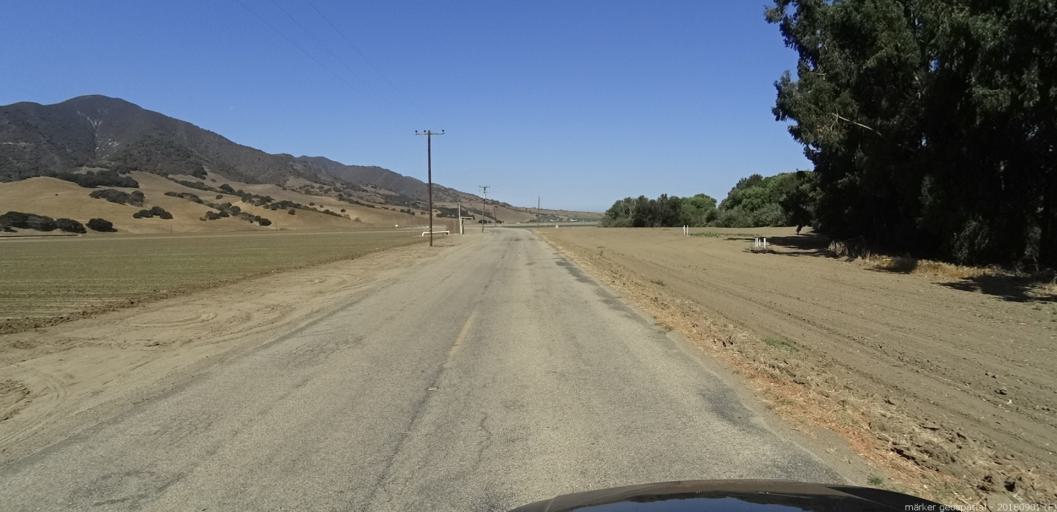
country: US
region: California
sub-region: Monterey County
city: Chualar
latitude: 36.5319
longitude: -121.5340
